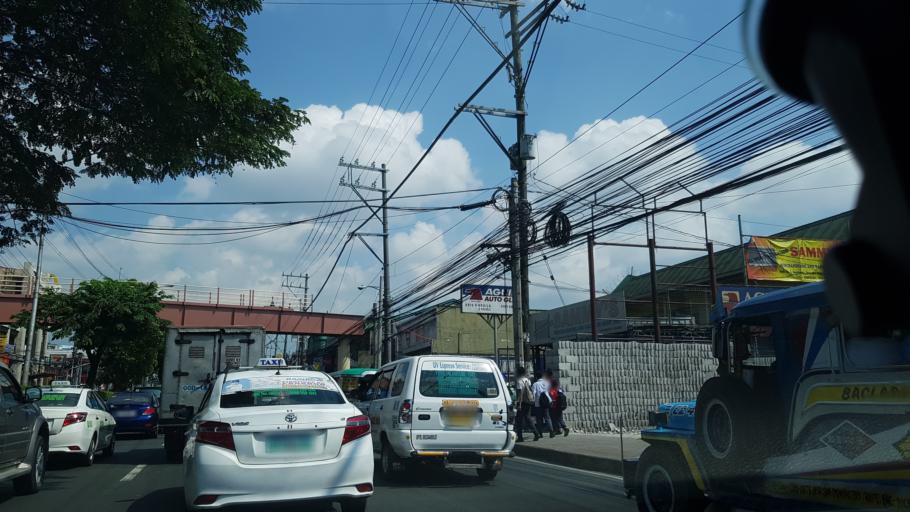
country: PH
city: Sambayanihan People's Village
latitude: 14.4716
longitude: 121.0069
